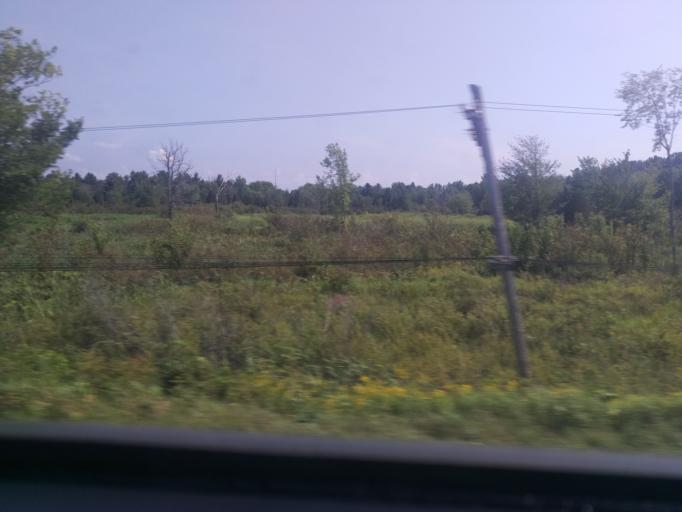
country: US
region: New York
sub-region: Jefferson County
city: Alexandria Bay
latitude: 44.4601
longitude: -75.9145
